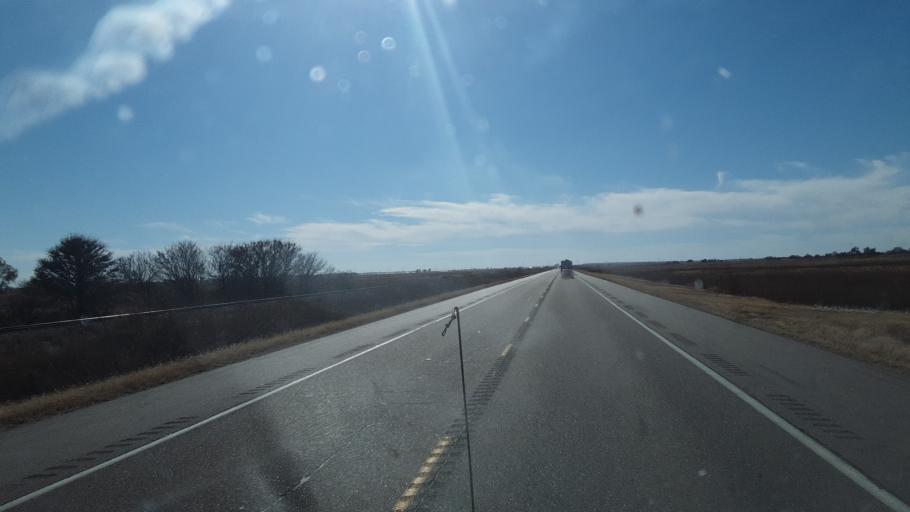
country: US
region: Kansas
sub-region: Pawnee County
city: Larned
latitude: 38.2456
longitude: -99.0142
